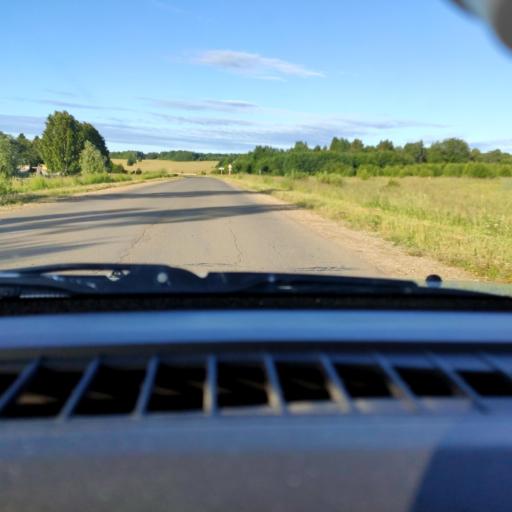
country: RU
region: Perm
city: Uinskoye
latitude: 57.0835
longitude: 56.5558
